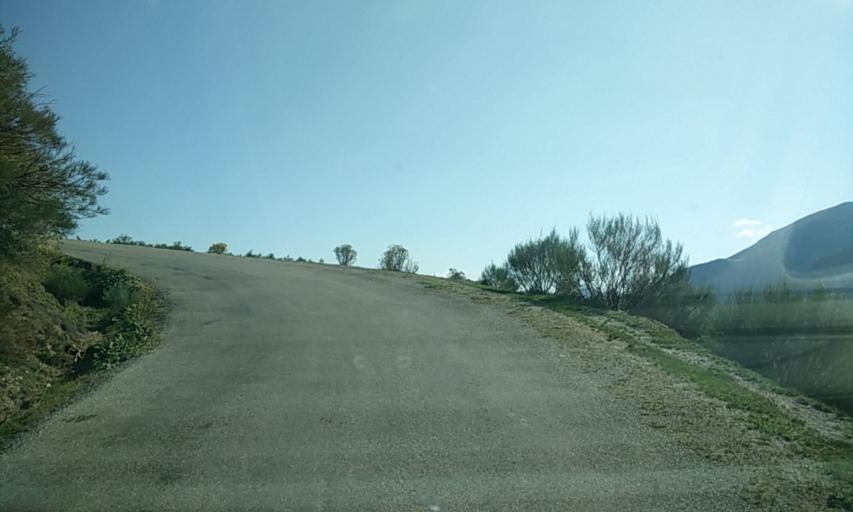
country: ES
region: Cantabria
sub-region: Provincia de Cantabria
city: Camaleno
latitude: 43.0705
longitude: -4.7612
